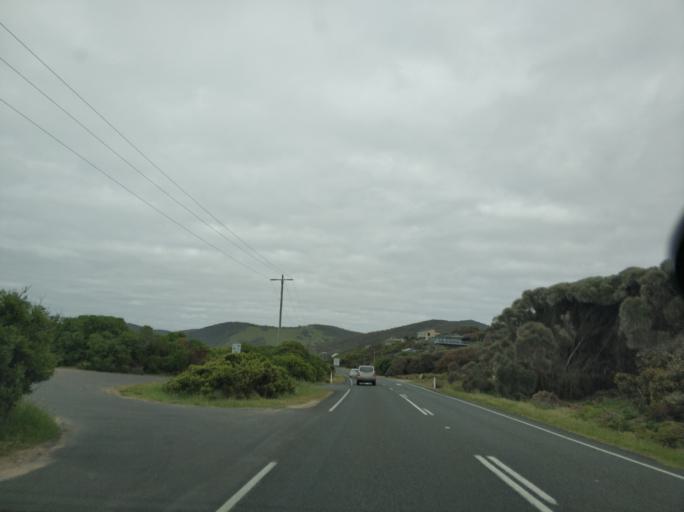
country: AU
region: Victoria
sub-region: Surf Coast
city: Anglesea
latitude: -38.4699
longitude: 144.0564
